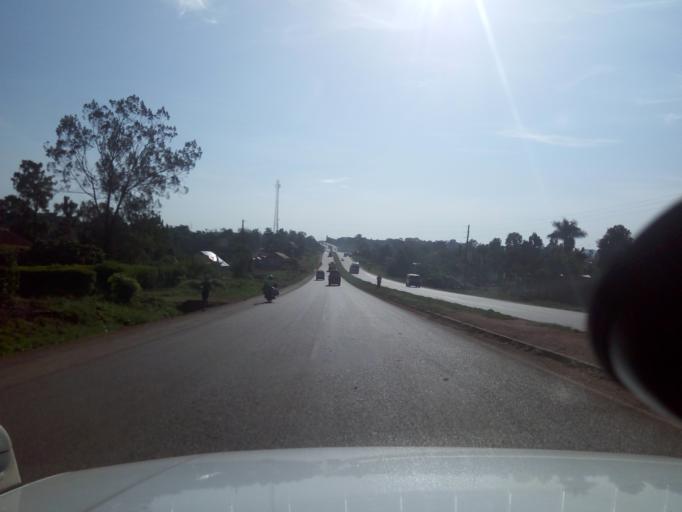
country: UG
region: Eastern Region
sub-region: Jinja District
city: Bugembe
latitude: 0.4744
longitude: 33.2602
